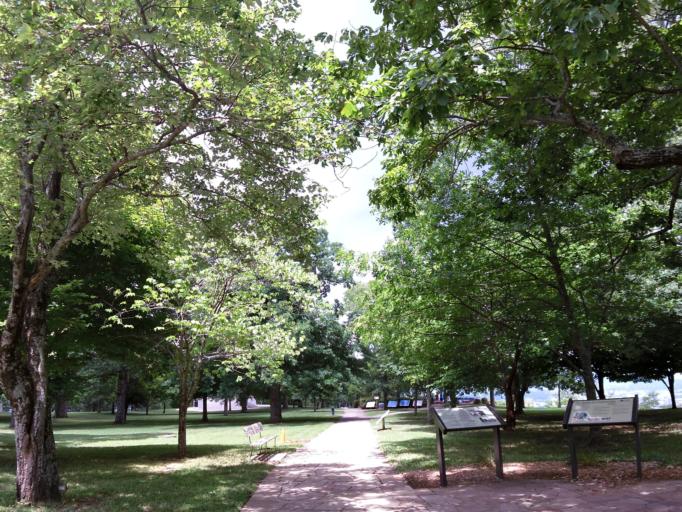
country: US
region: Tennessee
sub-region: Hamilton County
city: Lookout Mountain
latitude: 35.0099
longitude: -85.3438
